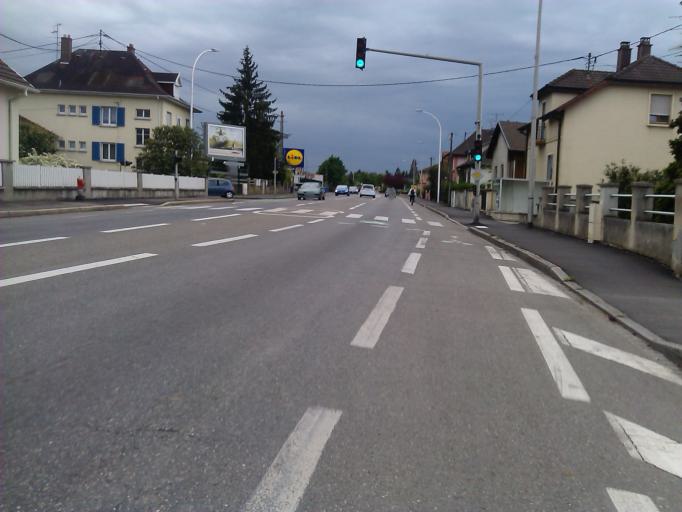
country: FR
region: Alsace
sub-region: Departement du Haut-Rhin
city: Kingersheim
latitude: 47.7978
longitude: 7.3361
